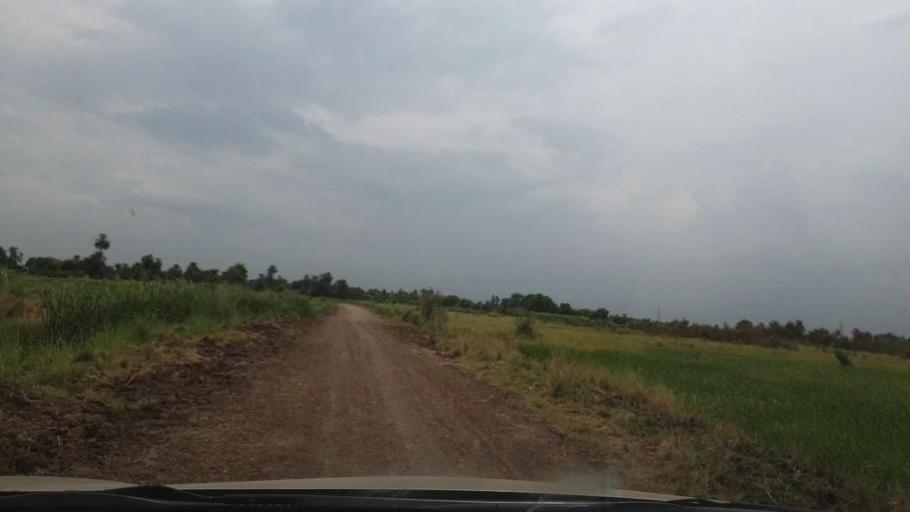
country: PK
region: Sindh
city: Ratodero
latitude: 27.7982
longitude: 68.3129
